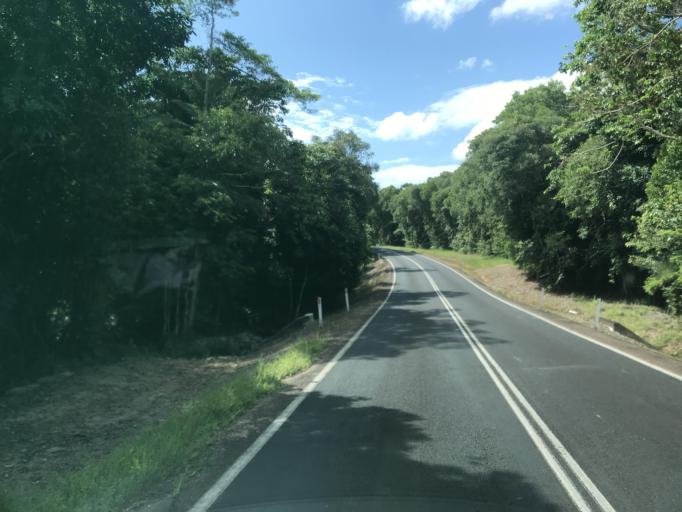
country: AU
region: Queensland
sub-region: Cassowary Coast
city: Innisfail
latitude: -17.8647
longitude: 146.0663
